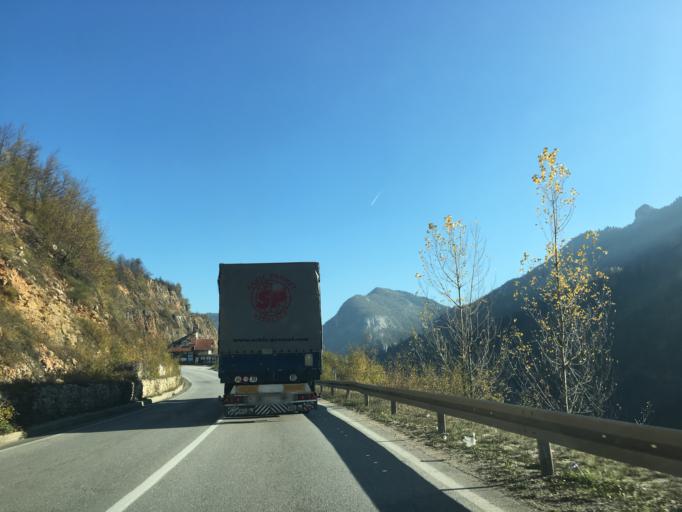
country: BA
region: Federation of Bosnia and Herzegovina
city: Kobilja Glava
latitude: 43.8449
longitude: 18.4741
